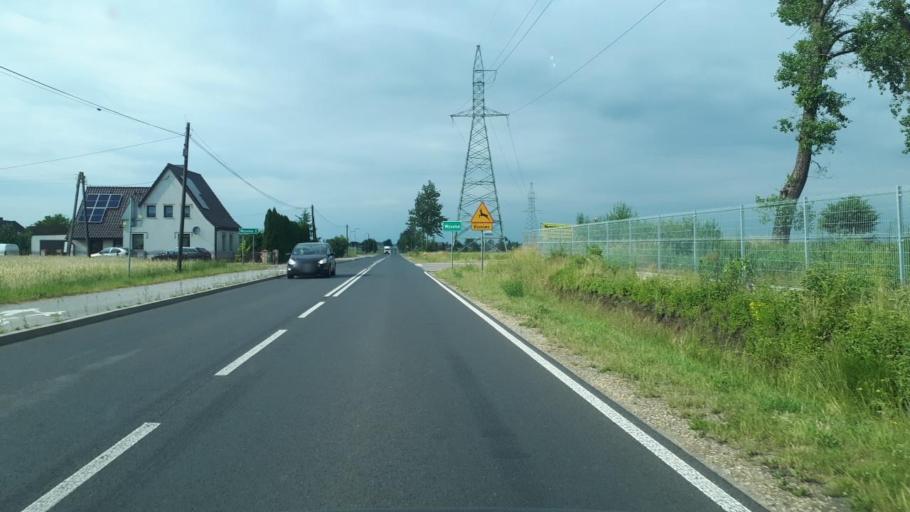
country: PL
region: Opole Voivodeship
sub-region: Powiat oleski
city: Olesno
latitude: 50.8446
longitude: 18.4131
